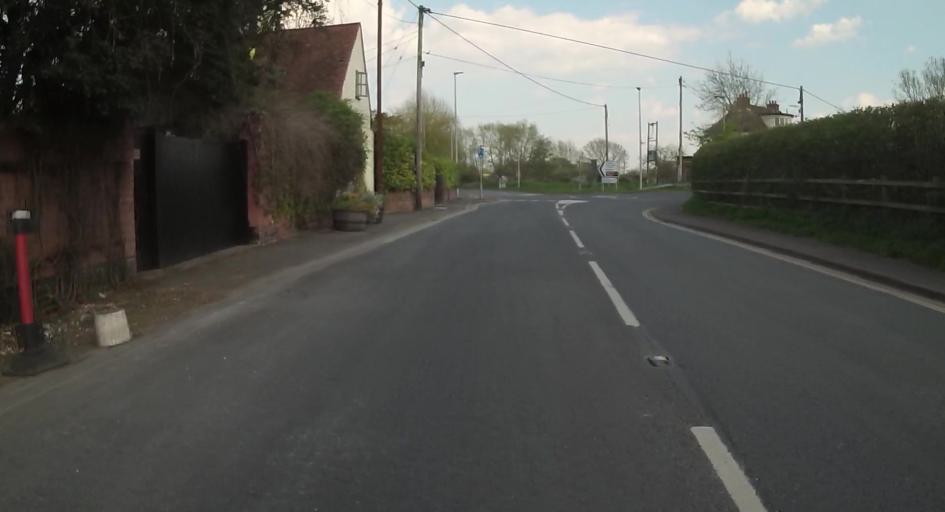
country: GB
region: England
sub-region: West Berkshire
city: Stratfield Mortimer
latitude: 51.3734
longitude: -1.0372
